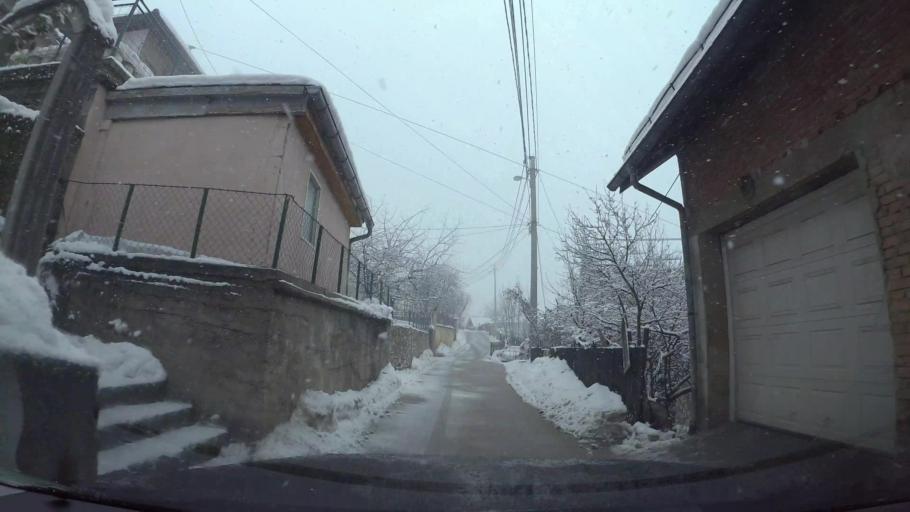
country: BA
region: Federation of Bosnia and Herzegovina
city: Kobilja Glava
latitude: 43.8530
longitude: 18.4496
